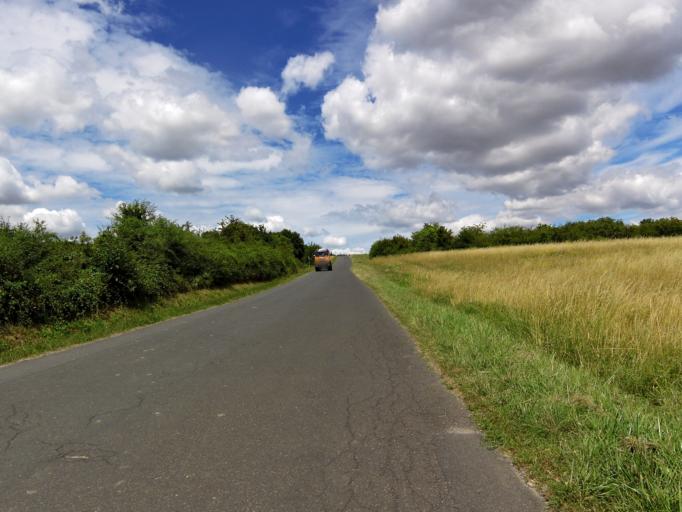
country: DE
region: Bavaria
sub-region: Regierungsbezirk Unterfranken
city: Veitshochheim
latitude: 49.8125
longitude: 9.9000
